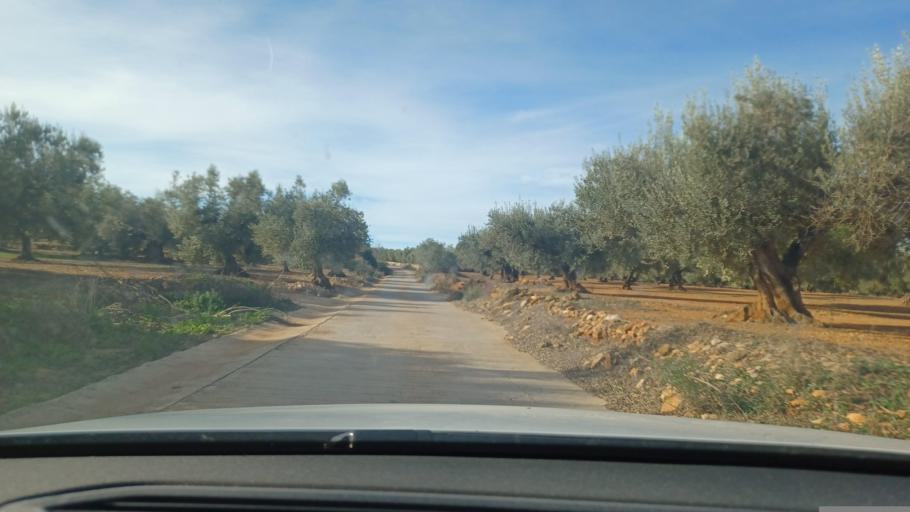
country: ES
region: Catalonia
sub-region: Provincia de Tarragona
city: Santa Barbara
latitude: 40.6901
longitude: 0.5053
